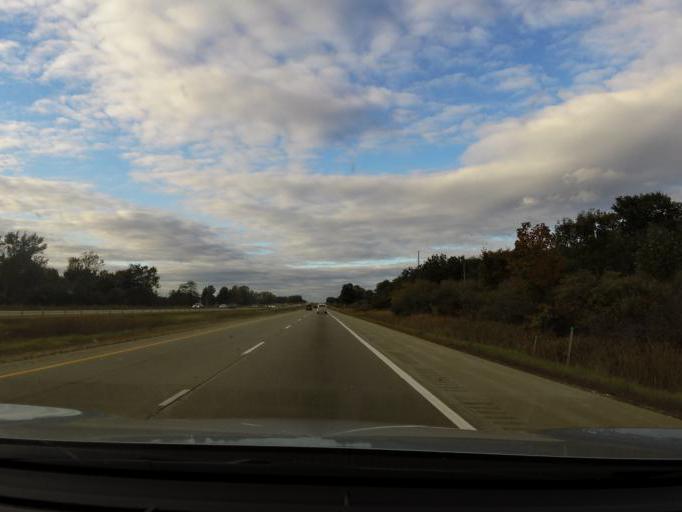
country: US
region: Michigan
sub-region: Genesee County
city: Linden
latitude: 42.7272
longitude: -83.7632
